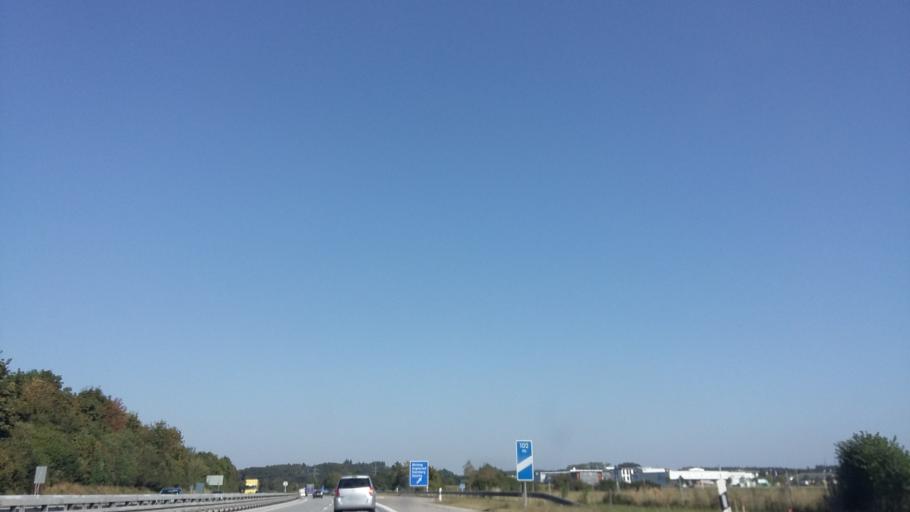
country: DE
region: Bavaria
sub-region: Upper Bavaria
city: Gilching
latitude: 48.0939
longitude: 11.2985
